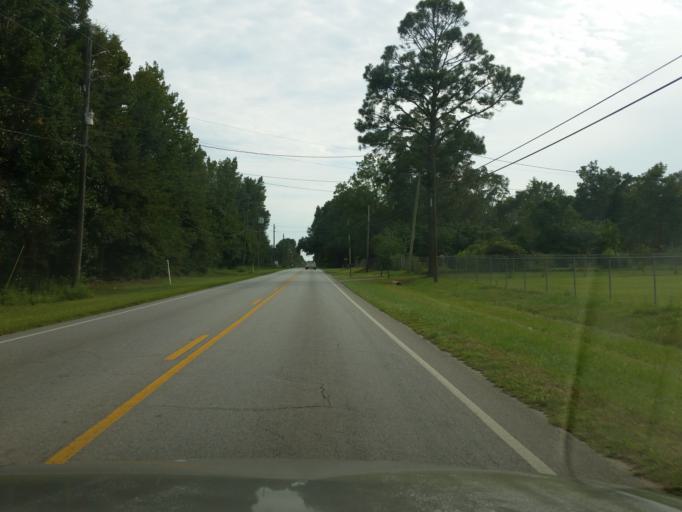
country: US
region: Florida
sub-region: Escambia County
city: Cantonment
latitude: 30.6349
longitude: -87.3197
